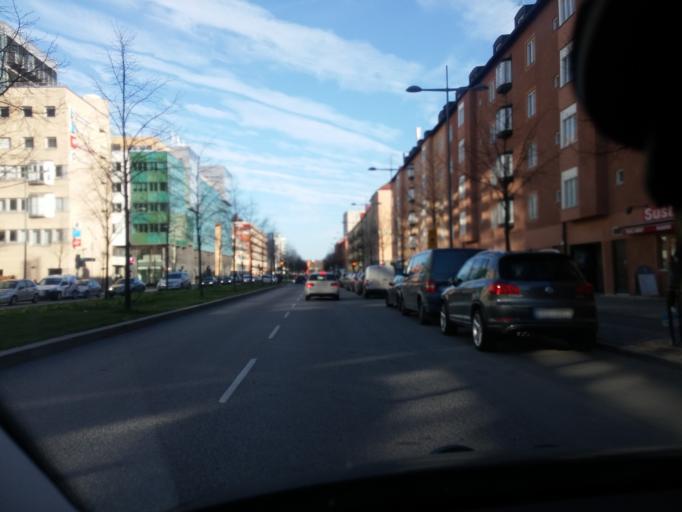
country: SE
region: Stockholm
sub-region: Solna Kommun
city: Solna
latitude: 59.3343
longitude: 18.0147
